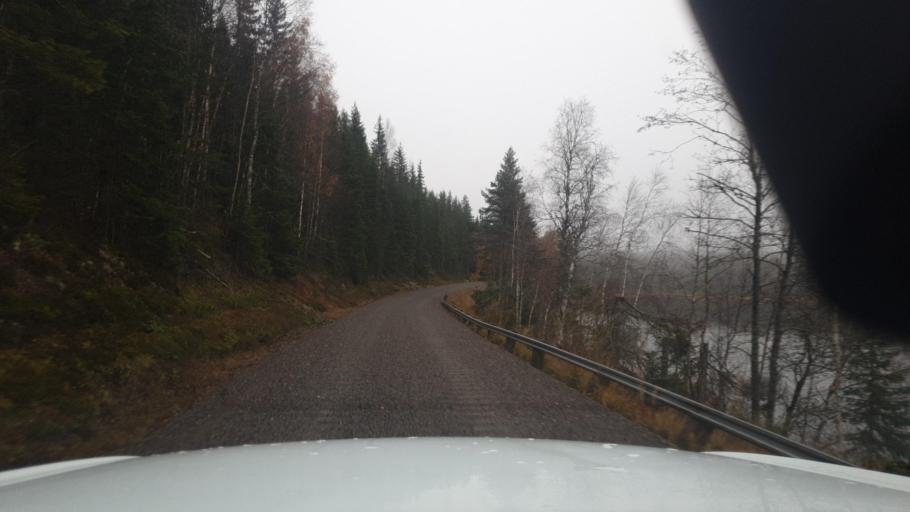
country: SE
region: Vaermland
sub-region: Eda Kommun
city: Charlottenberg
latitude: 60.1072
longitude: 12.6057
